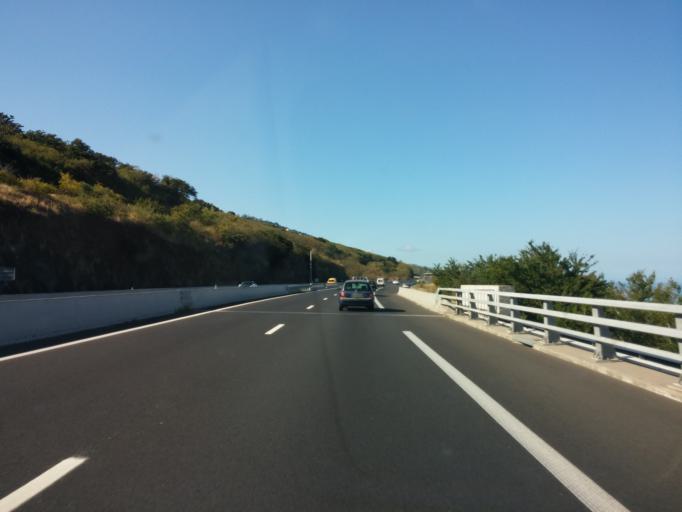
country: RE
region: Reunion
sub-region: Reunion
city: Trois-Bassins
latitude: -21.1186
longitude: 55.2780
